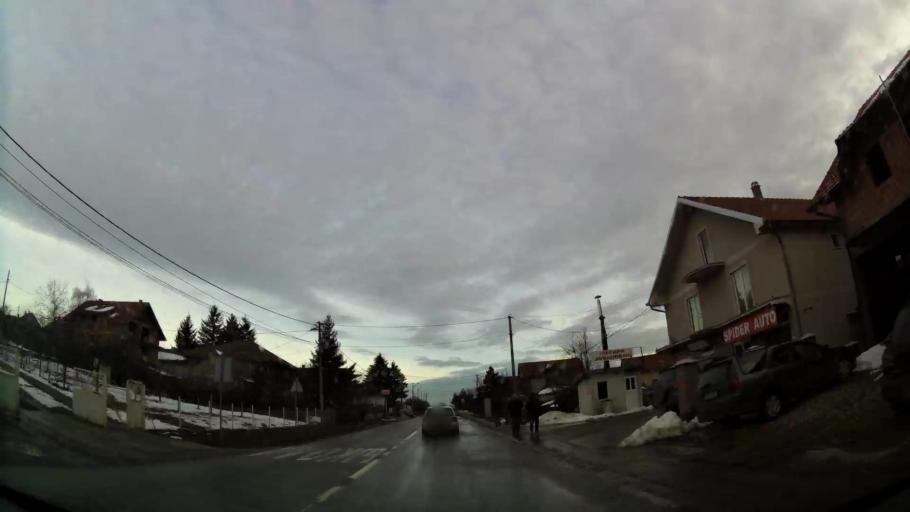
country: RS
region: Central Serbia
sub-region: Belgrade
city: Rakovica
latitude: 44.7218
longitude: 20.4977
